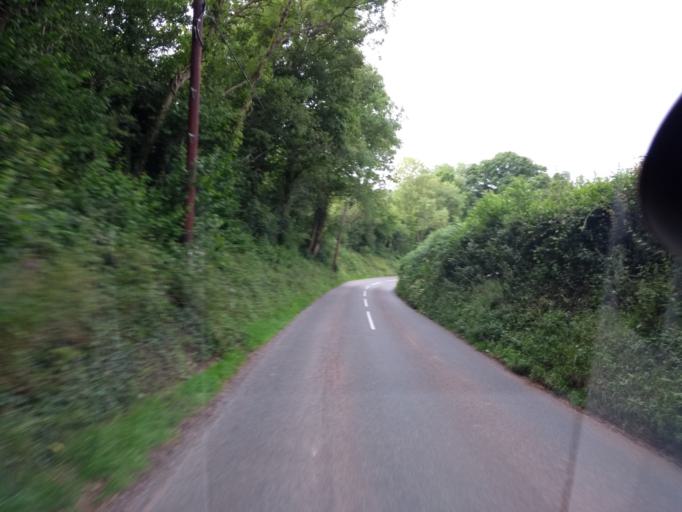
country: GB
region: England
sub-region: Somerset
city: Wiveliscombe
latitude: 51.0545
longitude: -3.2909
